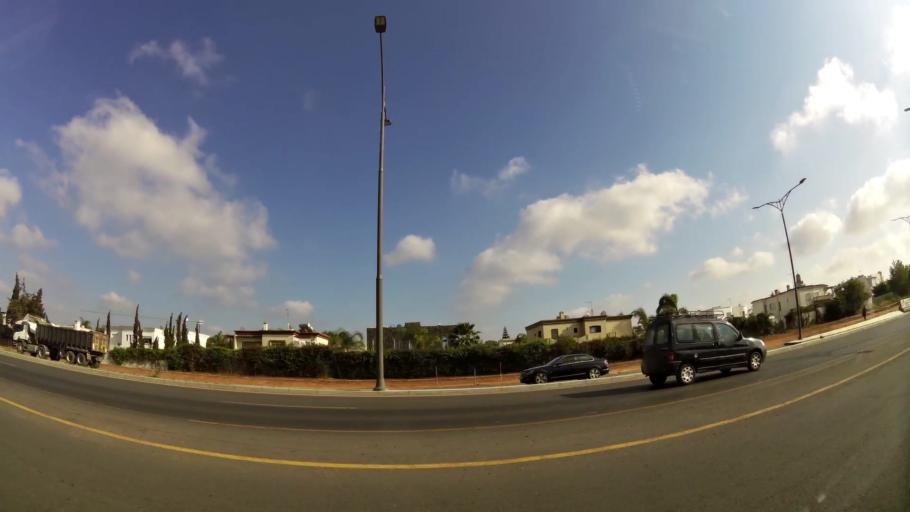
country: MA
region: Rabat-Sale-Zemmour-Zaer
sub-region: Skhirate-Temara
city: Temara
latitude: 33.9480
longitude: -6.8677
